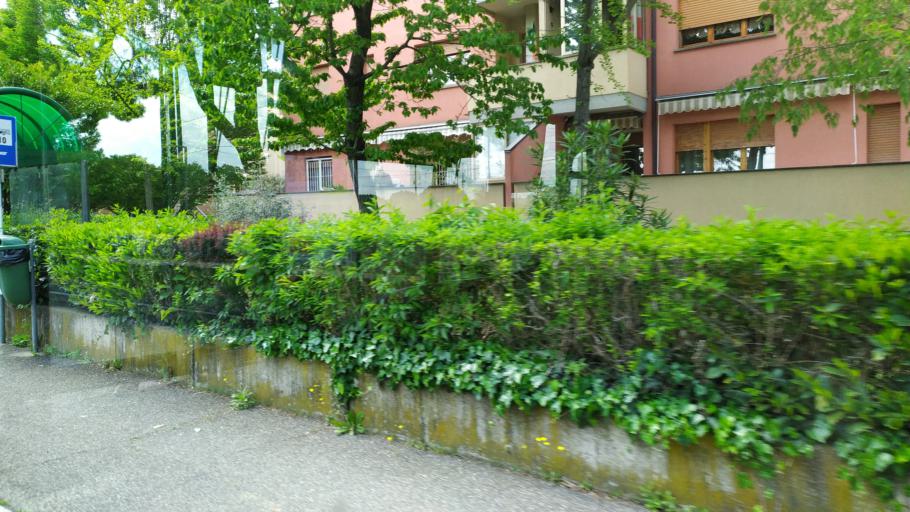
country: IT
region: Emilia-Romagna
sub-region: Provincia di Bologna
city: Imola
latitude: 44.3442
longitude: 11.6803
